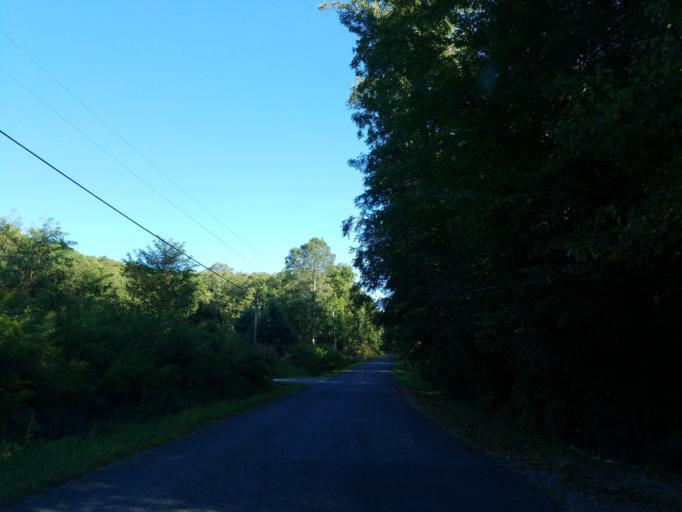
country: US
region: Georgia
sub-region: Gilmer County
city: Ellijay
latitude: 34.6449
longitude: -84.2853
